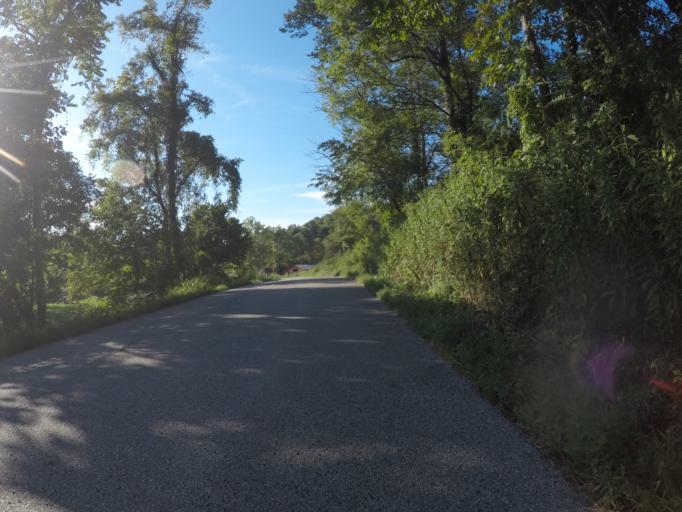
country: US
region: West Virginia
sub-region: Cabell County
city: Huntington
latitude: 38.5110
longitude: -82.4952
